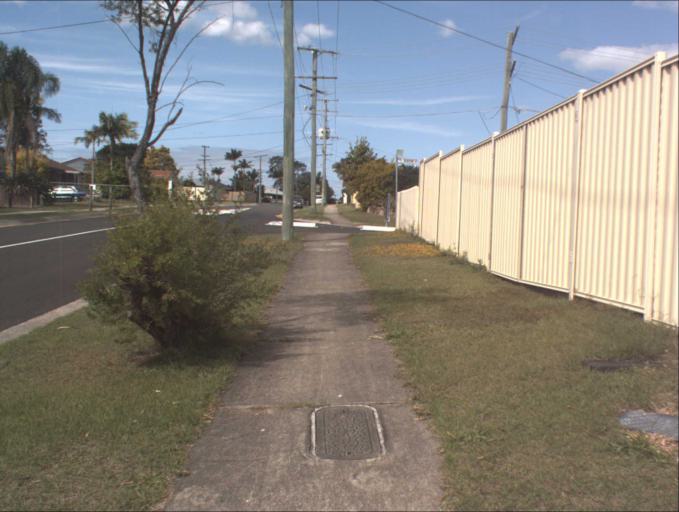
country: AU
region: Queensland
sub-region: Logan
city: Logan Reserve
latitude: -27.6856
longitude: 153.0814
